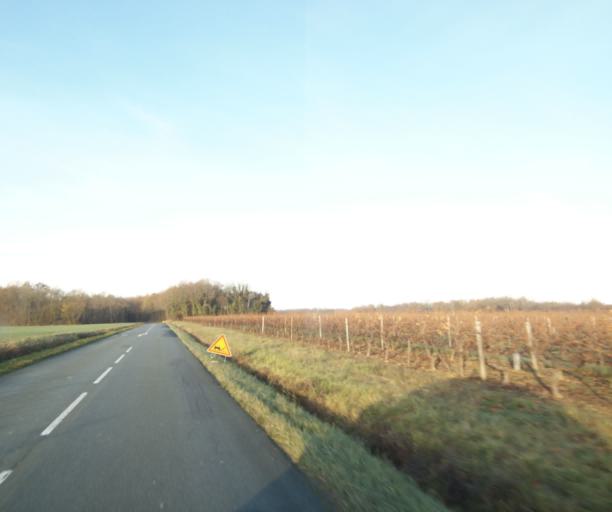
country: FR
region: Poitou-Charentes
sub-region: Departement de la Charente-Maritime
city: Fontcouverte
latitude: 45.7767
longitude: -0.5567
